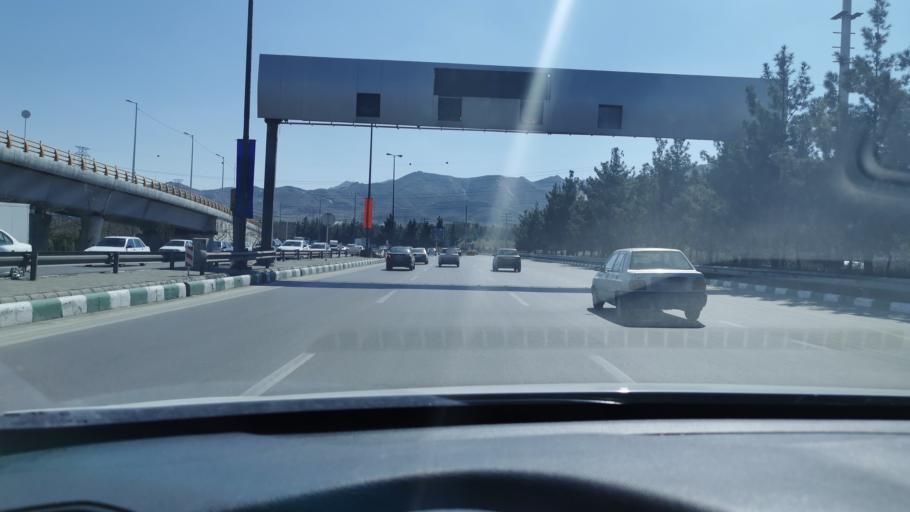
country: IR
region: Razavi Khorasan
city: Mashhad
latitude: 36.2762
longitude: 59.5549
